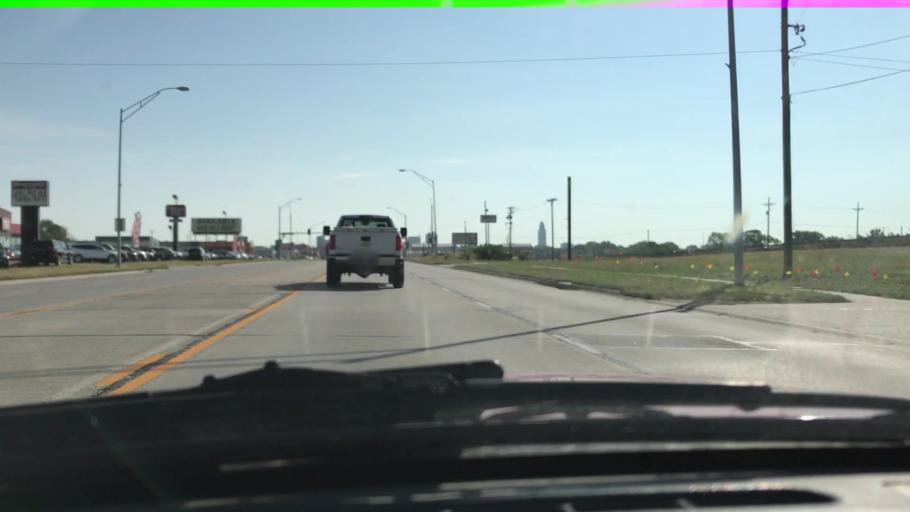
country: US
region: Nebraska
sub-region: Lancaster County
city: Lincoln
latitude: 40.8137
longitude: -96.7350
